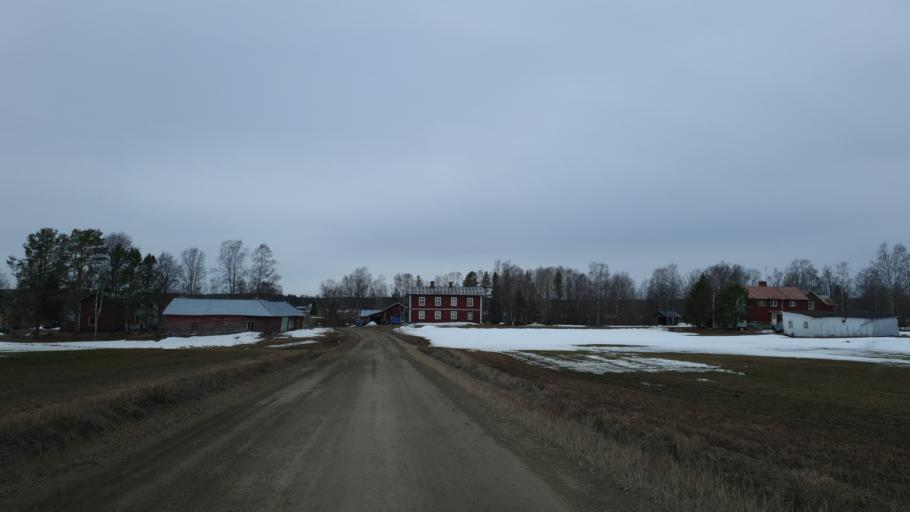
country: SE
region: Vaesterbotten
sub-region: Robertsfors Kommun
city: Robertsfors
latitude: 64.3829
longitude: 20.9215
